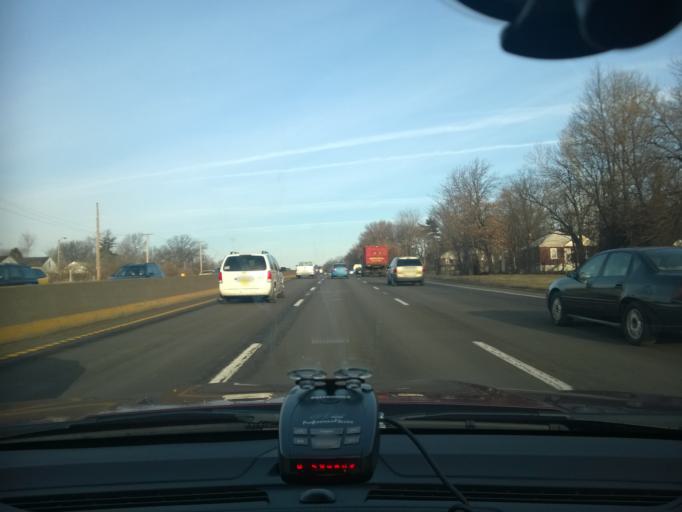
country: US
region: Missouri
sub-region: Saint Louis County
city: Northwoods
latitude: 38.7072
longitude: -90.2752
